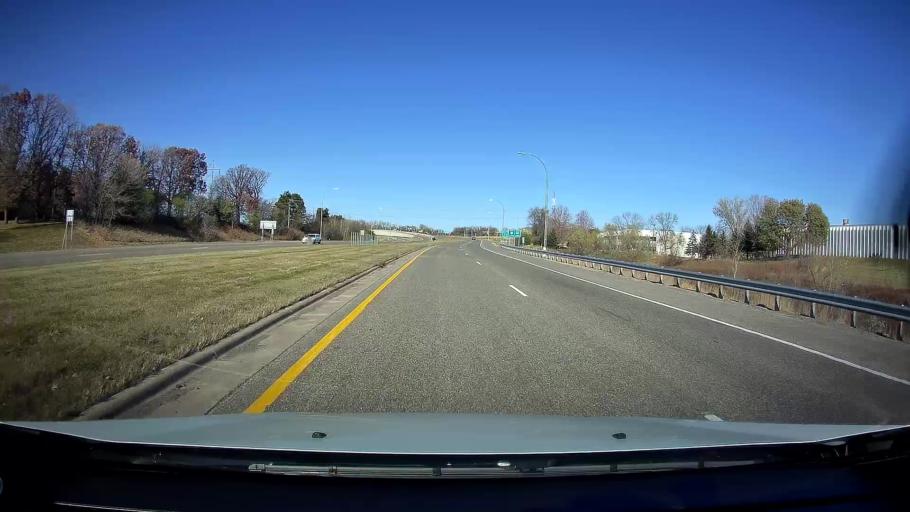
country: US
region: Minnesota
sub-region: Ramsey County
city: Arden Hills
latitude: 45.0562
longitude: -93.1570
